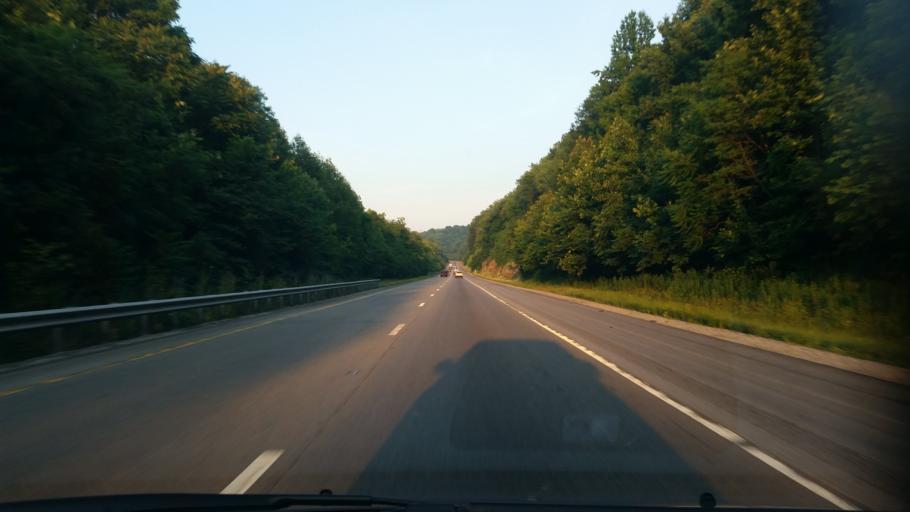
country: US
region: Tennessee
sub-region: Putnam County
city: Algood
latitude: 36.1458
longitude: -85.4051
